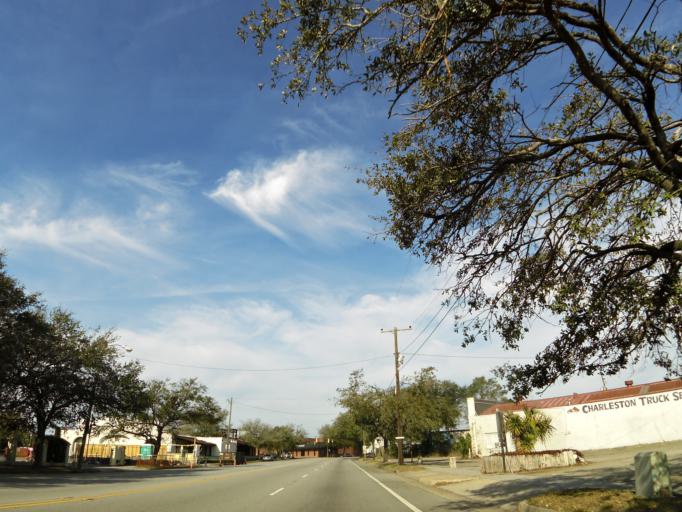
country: US
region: South Carolina
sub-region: Charleston County
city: Charleston
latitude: 32.8098
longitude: -79.9463
